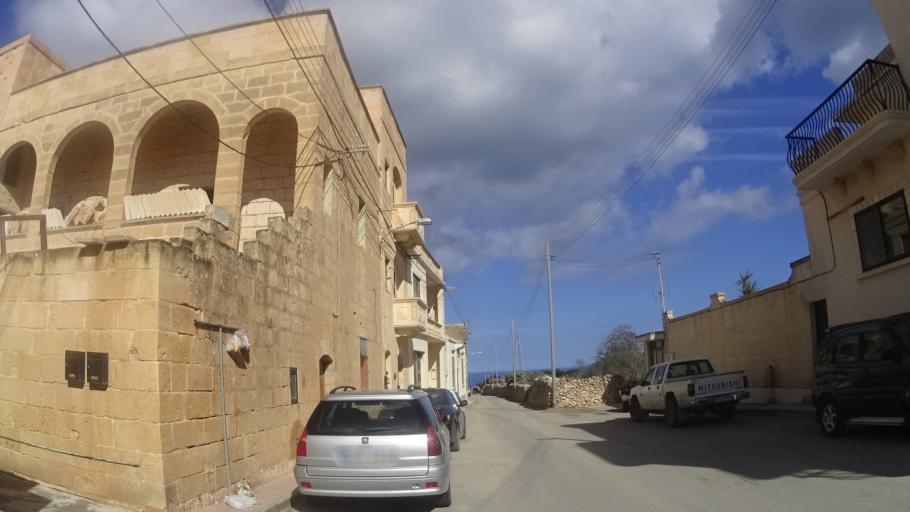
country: MT
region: In-Nadur
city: Nadur
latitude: 36.0500
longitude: 14.3001
